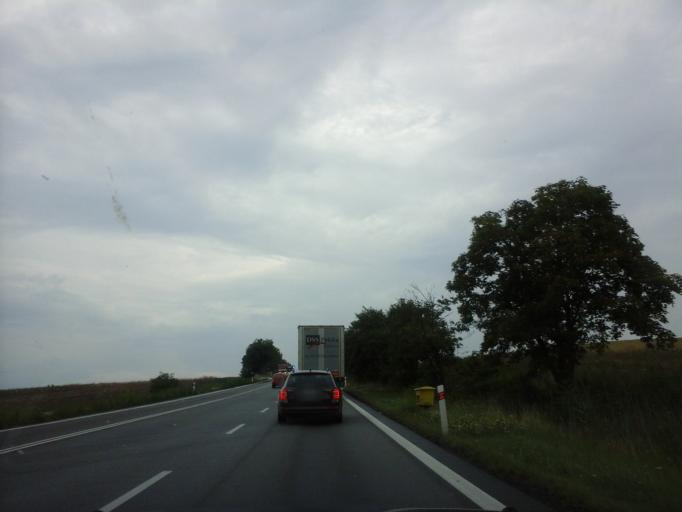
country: CZ
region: South Moravian
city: Svitavka
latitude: 49.4780
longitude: 16.5829
